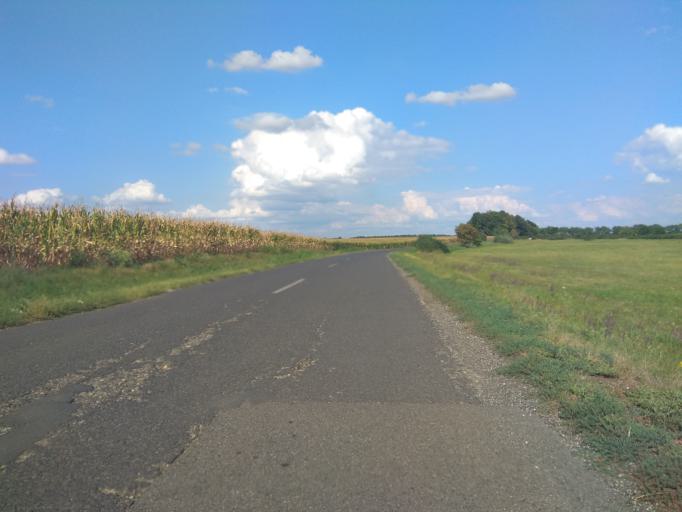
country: HU
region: Borsod-Abauj-Zemplen
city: Mezokeresztes
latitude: 47.8181
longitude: 20.7440
